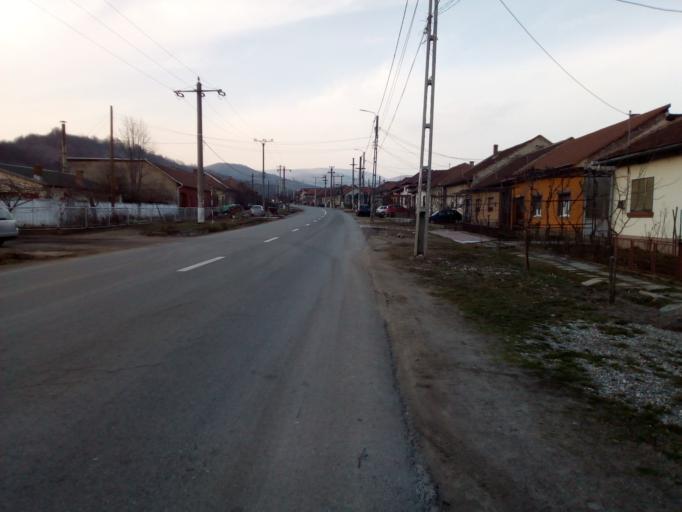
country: RO
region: Mehedinti
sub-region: Comuna Eselnita
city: Eselnita
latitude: 44.6934
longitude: 22.3653
